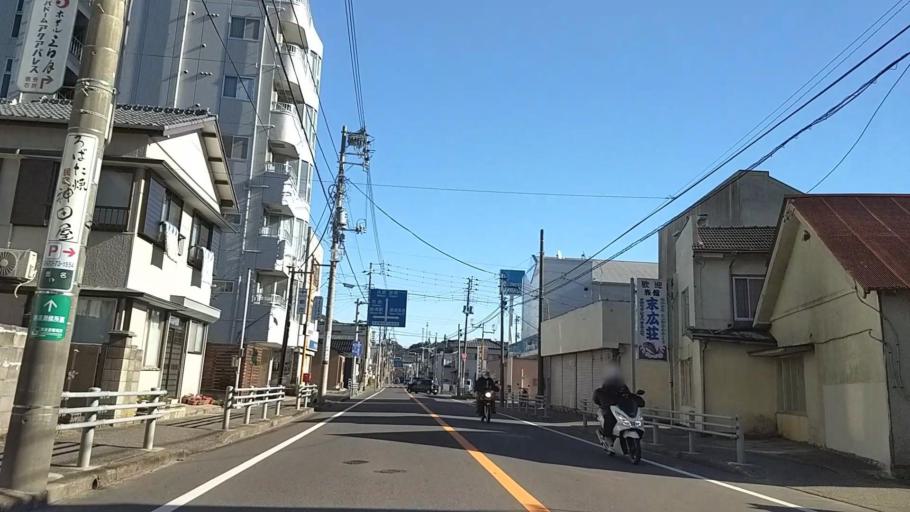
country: JP
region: Chiba
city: Katsuura
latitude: 35.1508
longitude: 140.3098
